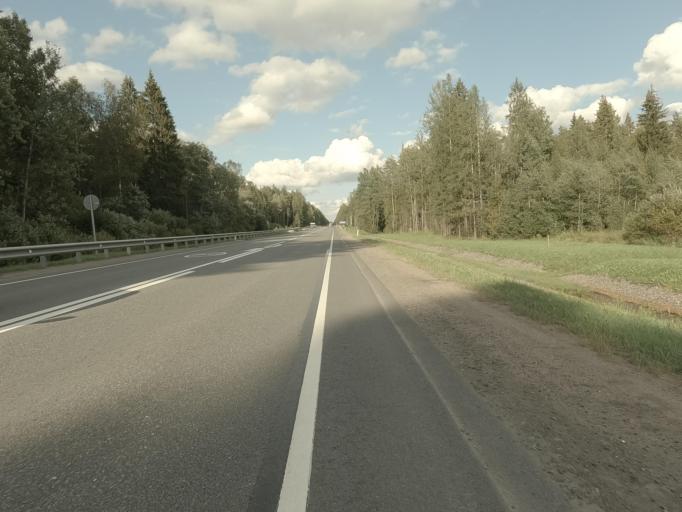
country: RU
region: Leningrad
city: Mga
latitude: 59.6941
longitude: 30.9828
